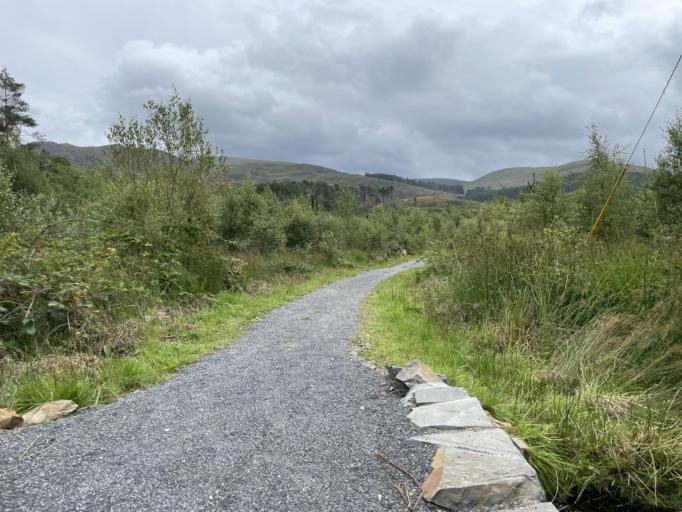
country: GB
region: Scotland
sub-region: Dumfries and Galloway
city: Newton Stewart
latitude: 55.0870
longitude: -4.5040
